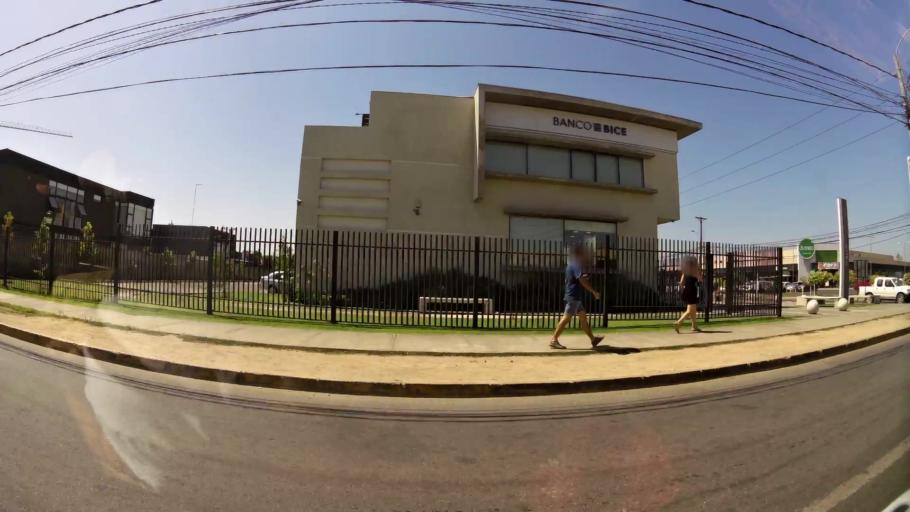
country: CL
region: Maule
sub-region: Provincia de Talca
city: Talca
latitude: -35.4312
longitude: -71.6278
